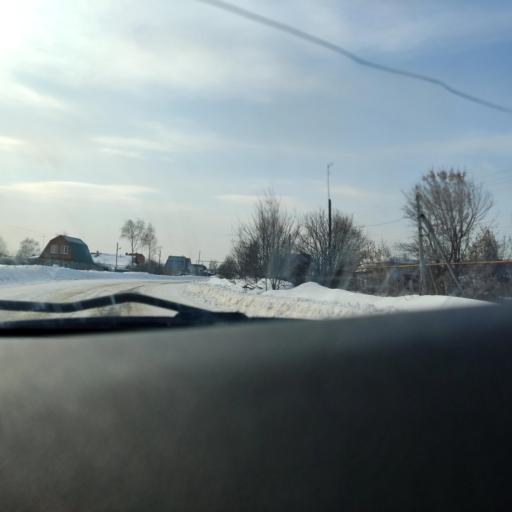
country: RU
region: Samara
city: Novokuybyshevsk
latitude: 53.2426
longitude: 49.8727
